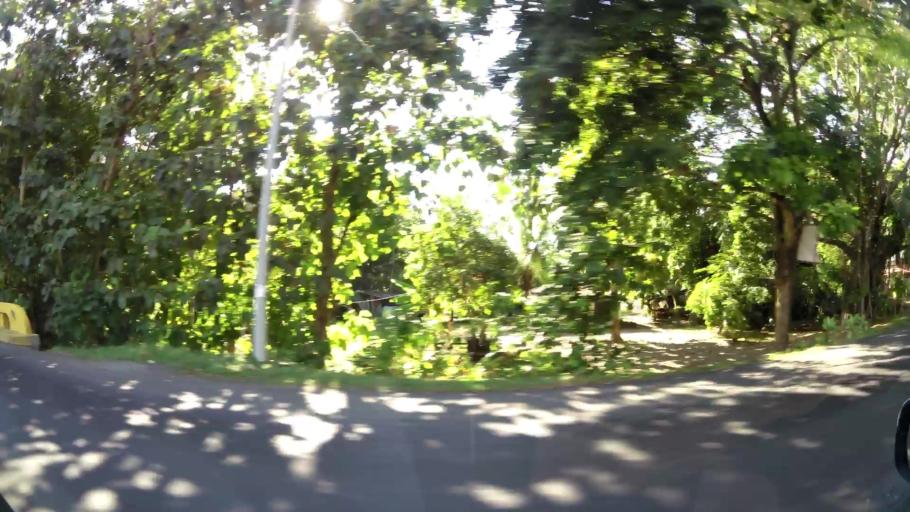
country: CR
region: Puntarenas
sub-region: Canton de Garabito
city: Jaco
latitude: 9.6103
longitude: -84.6164
